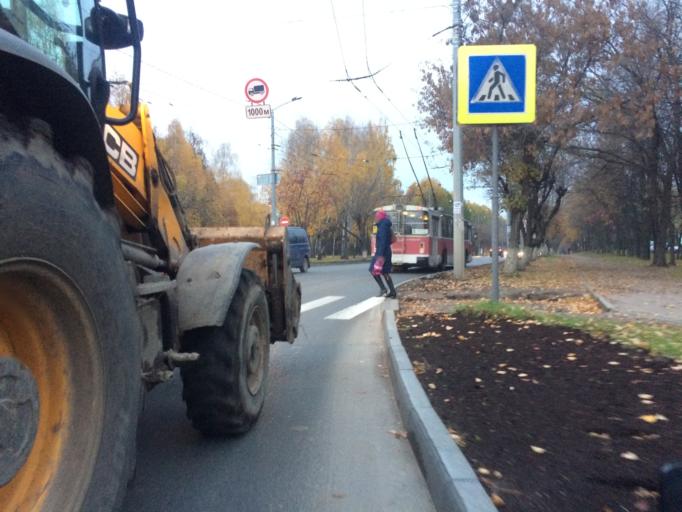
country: RU
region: Mariy-El
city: Yoshkar-Ola
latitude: 56.6108
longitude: 47.8800
